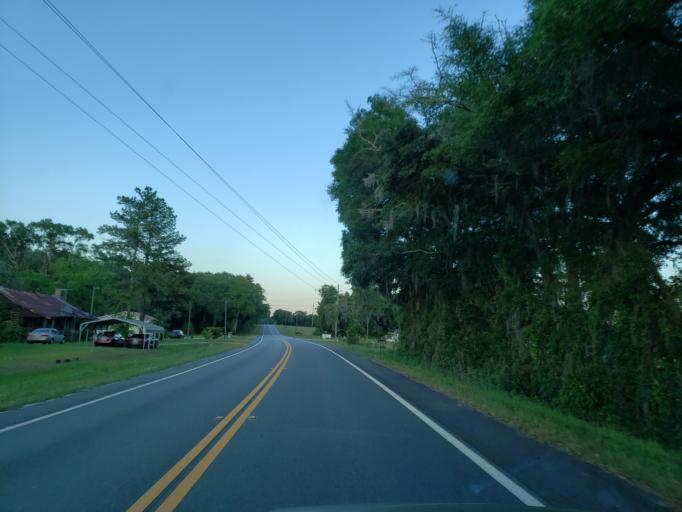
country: US
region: Georgia
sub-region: Echols County
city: Statenville
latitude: 30.5807
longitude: -83.1925
